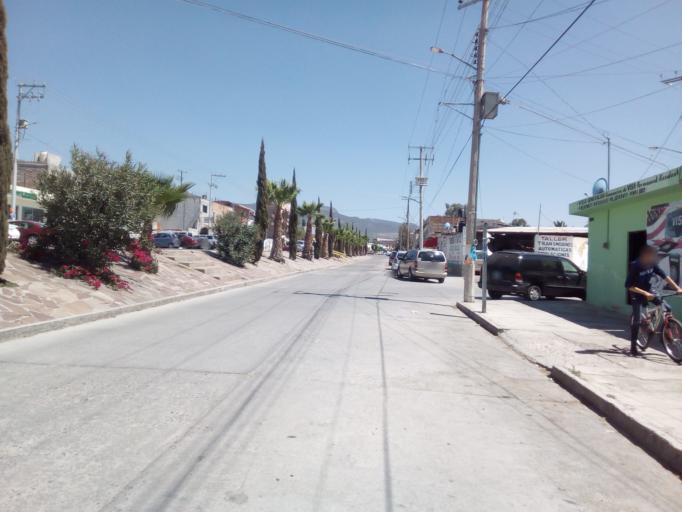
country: MX
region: Guanajuato
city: San Jose Iturbide
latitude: 21.0071
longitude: -100.3859
